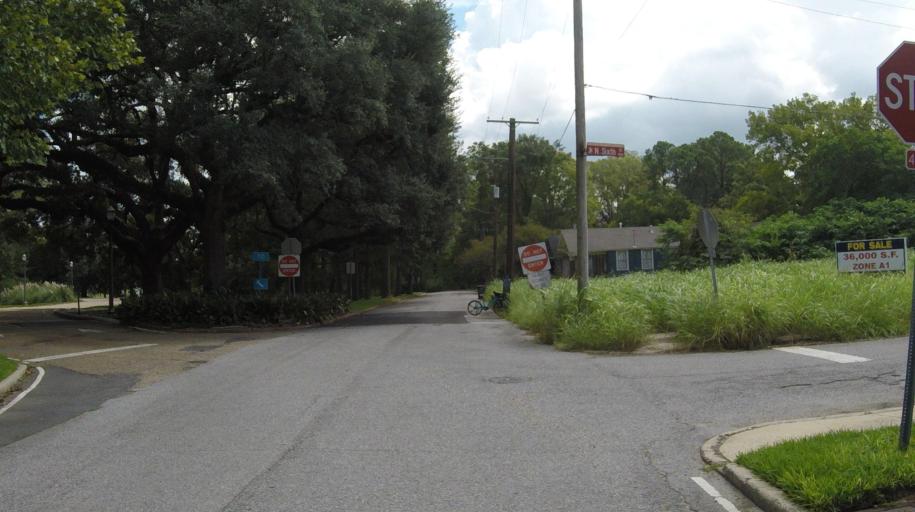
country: US
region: Louisiana
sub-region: West Baton Rouge Parish
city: Port Allen
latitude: 30.4568
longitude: -91.1849
